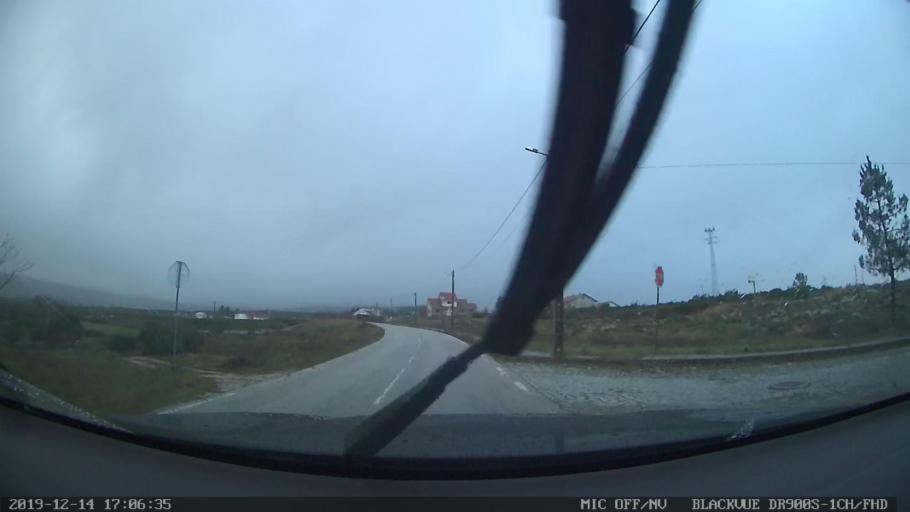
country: PT
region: Vila Real
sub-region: Vila Pouca de Aguiar
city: Vila Pouca de Aguiar
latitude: 41.4565
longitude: -7.5936
